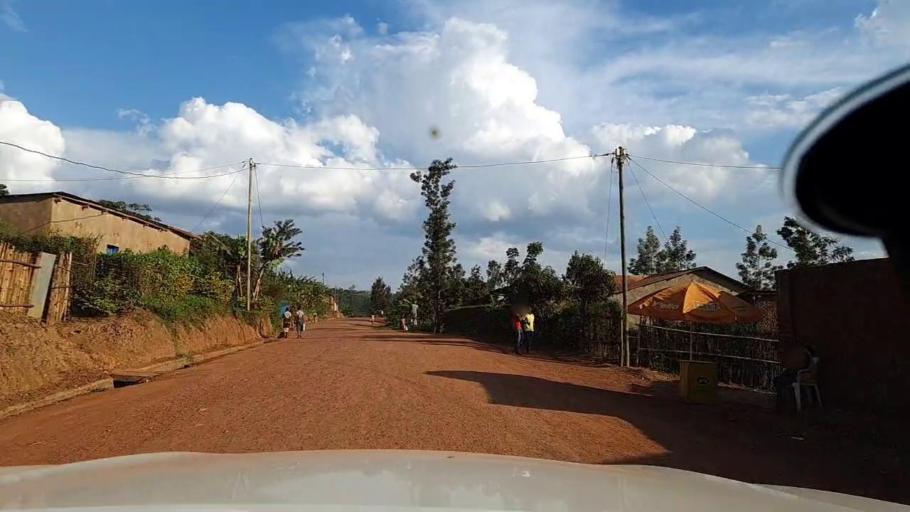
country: RW
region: Kigali
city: Kigali
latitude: -1.9121
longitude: 29.9840
